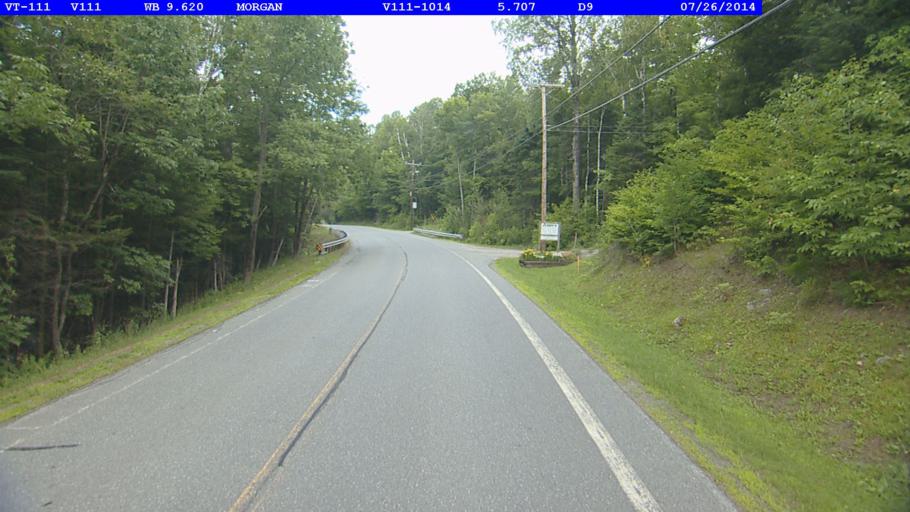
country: US
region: Vermont
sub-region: Orleans County
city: Newport
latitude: 44.8989
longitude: -71.9736
